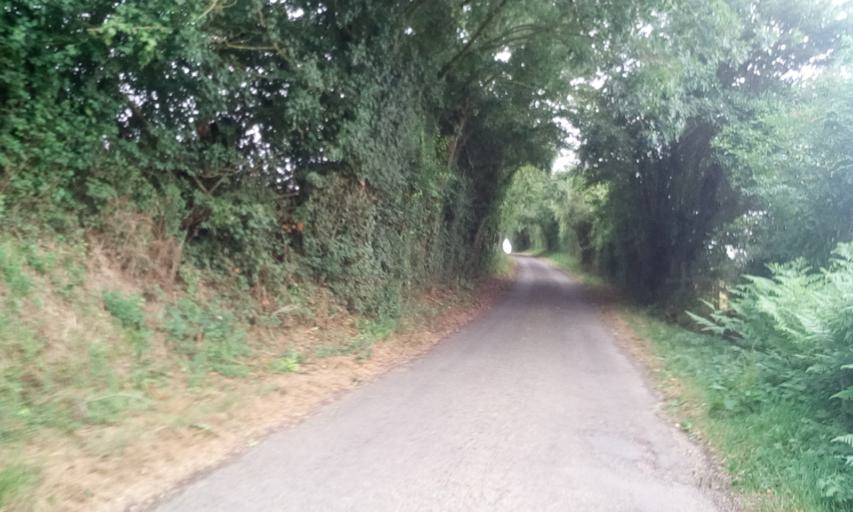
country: FR
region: Lower Normandy
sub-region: Departement du Calvados
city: Thury-Harcourt
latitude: 49.0054
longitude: -0.4409
